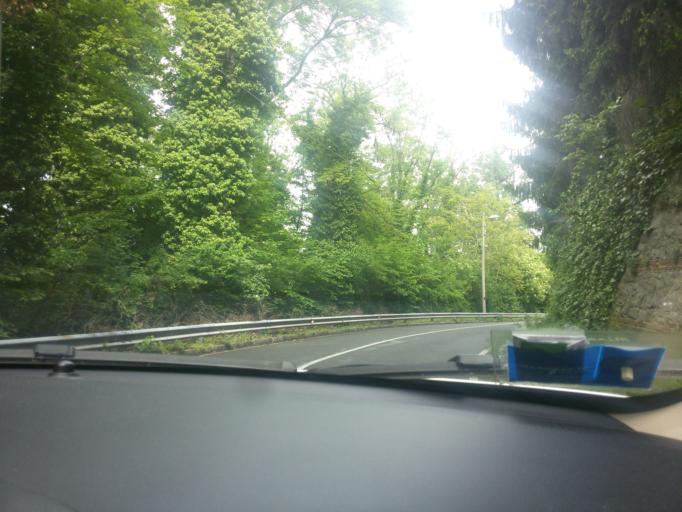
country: IT
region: Piedmont
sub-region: Provincia di Torino
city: Turin
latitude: 45.0482
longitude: 7.6935
